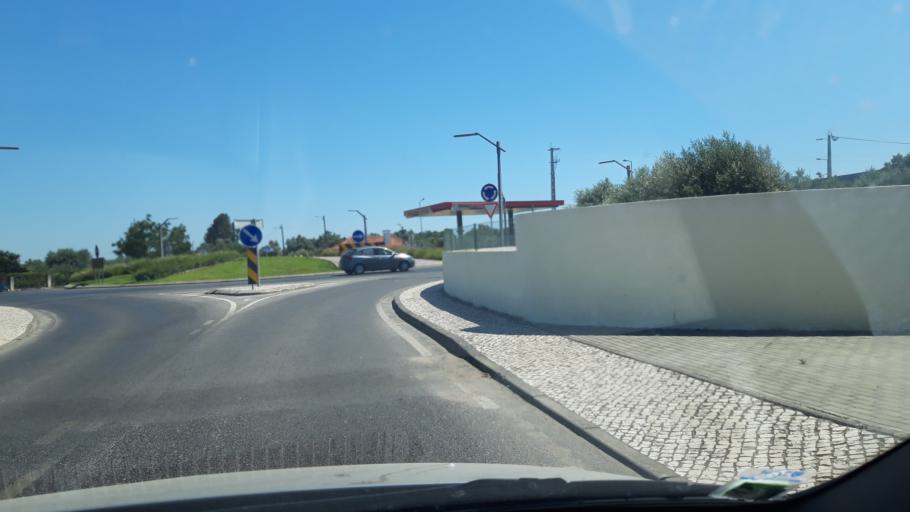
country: PT
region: Santarem
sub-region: Entroncamento
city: Entroncamento
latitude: 39.4625
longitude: -8.4519
